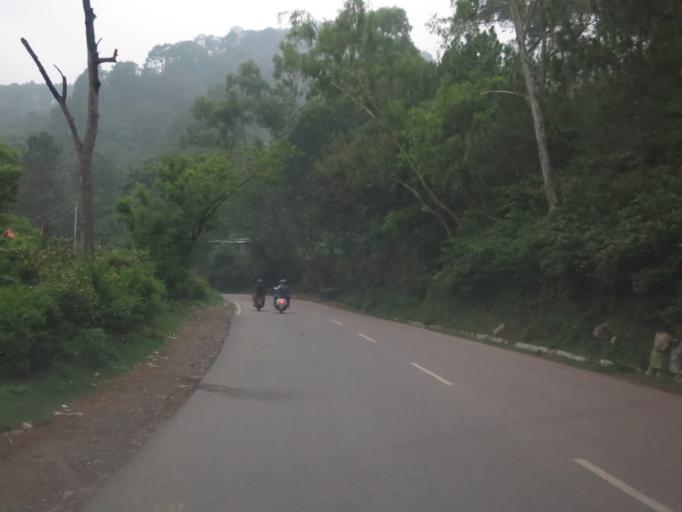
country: IN
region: Himachal Pradesh
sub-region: Solan
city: Dagshai
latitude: 30.8983
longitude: 77.0142
